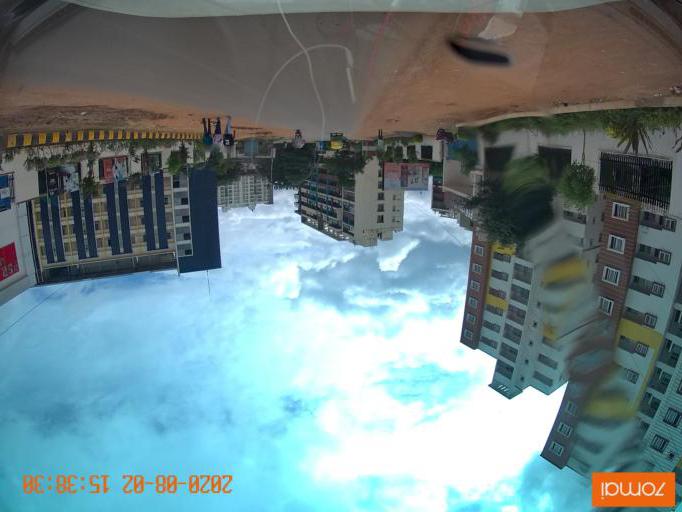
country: IN
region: Karnataka
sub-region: Bangalore Urban
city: Anekal
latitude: 12.8401
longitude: 77.6443
